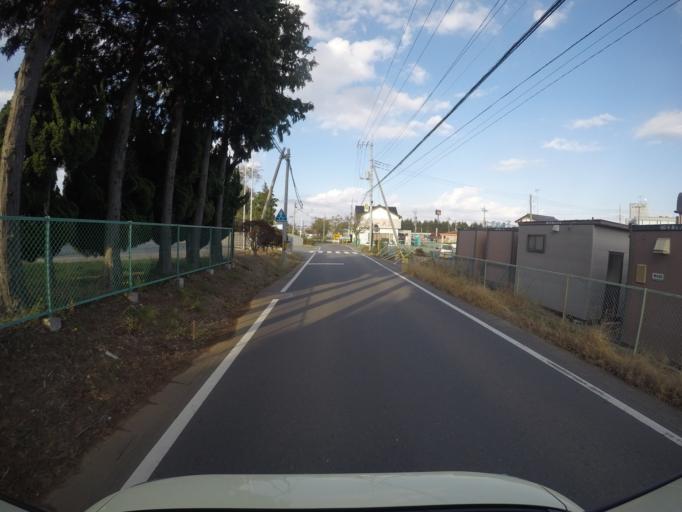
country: JP
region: Ibaraki
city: Naka
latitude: 36.0524
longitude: 140.0841
